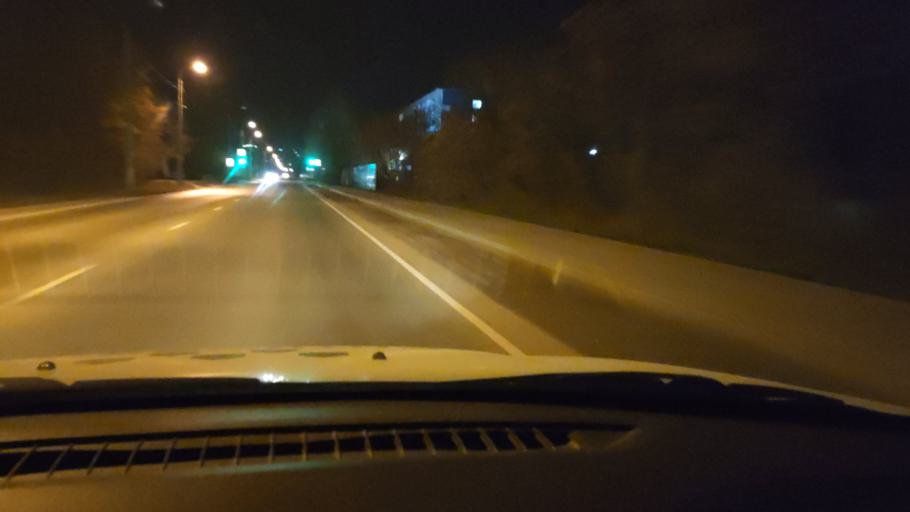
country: RU
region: Perm
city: Kondratovo
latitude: 57.9762
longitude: 56.1294
